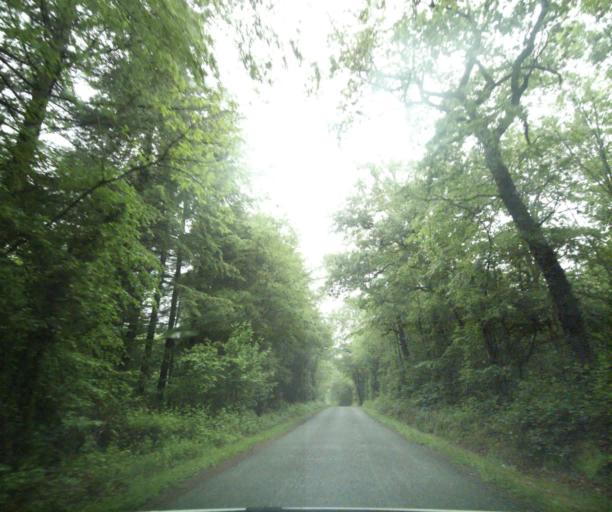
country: FR
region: Bourgogne
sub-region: Departement de Saone-et-Loire
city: Paray-le-Monial
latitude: 46.4192
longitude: 4.1948
